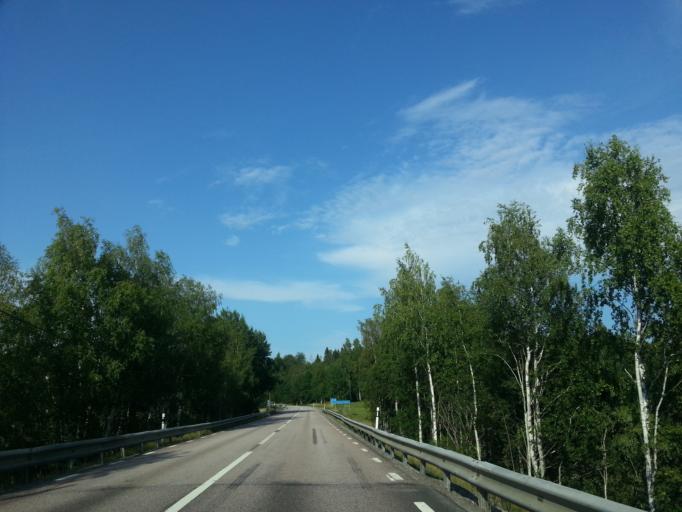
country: SE
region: Vaestmanland
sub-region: Skinnskattebergs Kommun
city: Skinnskatteberg
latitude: 59.8807
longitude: 15.6644
